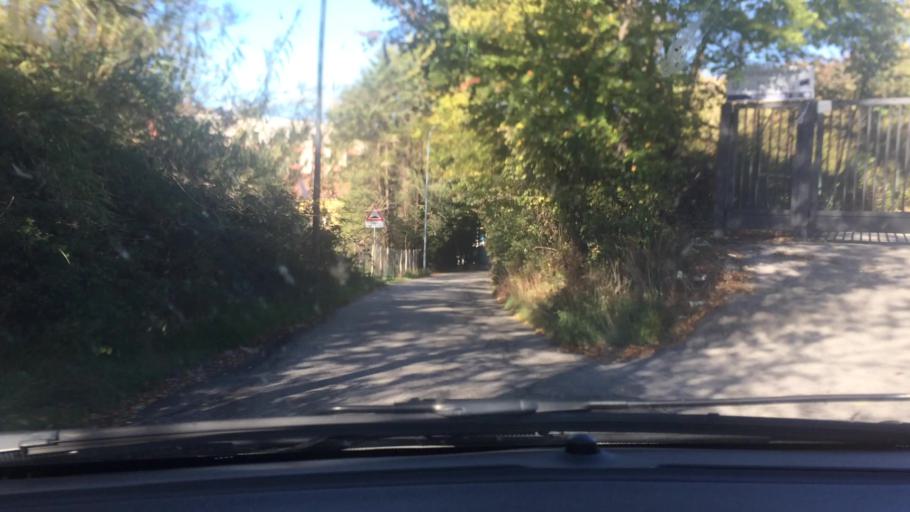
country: IT
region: Basilicate
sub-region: Provincia di Potenza
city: Potenza
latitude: 40.6421
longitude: 15.7927
